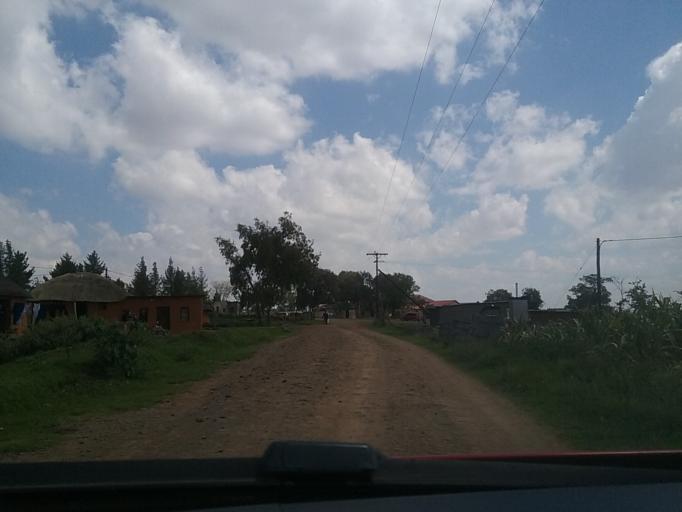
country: LS
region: Berea
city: Teyateyaneng
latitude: -29.2082
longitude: 27.8360
